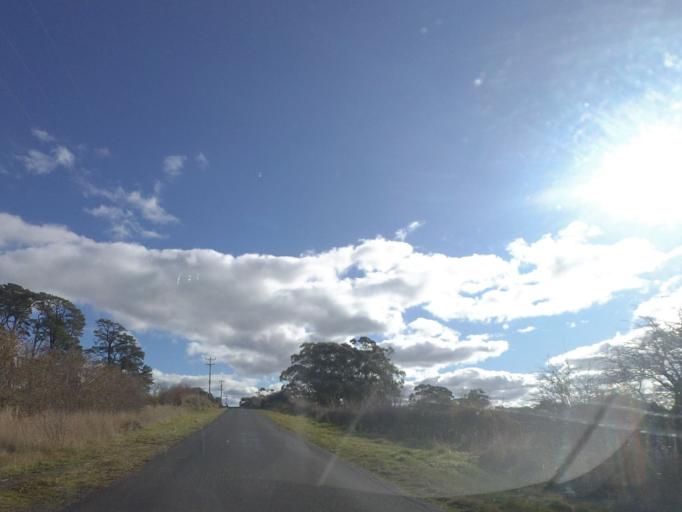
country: AU
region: Victoria
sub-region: Mount Alexander
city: Castlemaine
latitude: -37.2529
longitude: 144.4155
